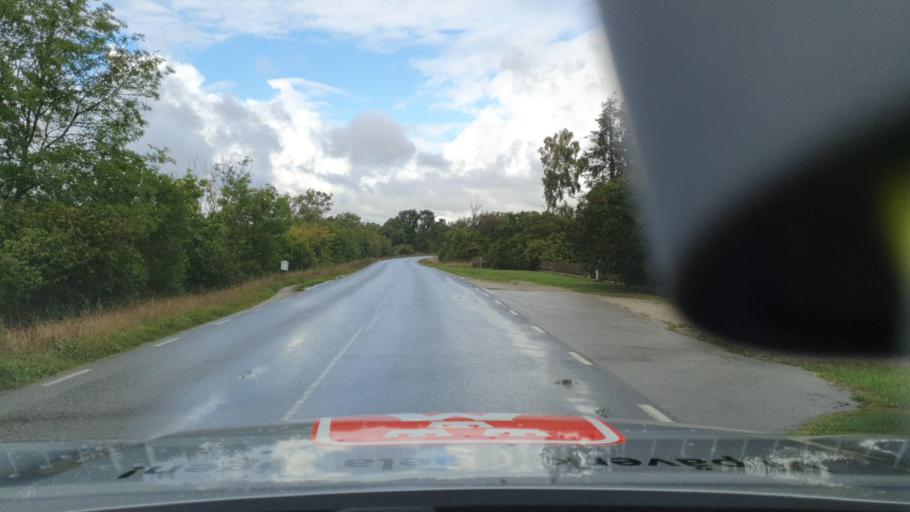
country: SE
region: Gotland
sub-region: Gotland
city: Hemse
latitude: 56.9746
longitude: 18.2359
